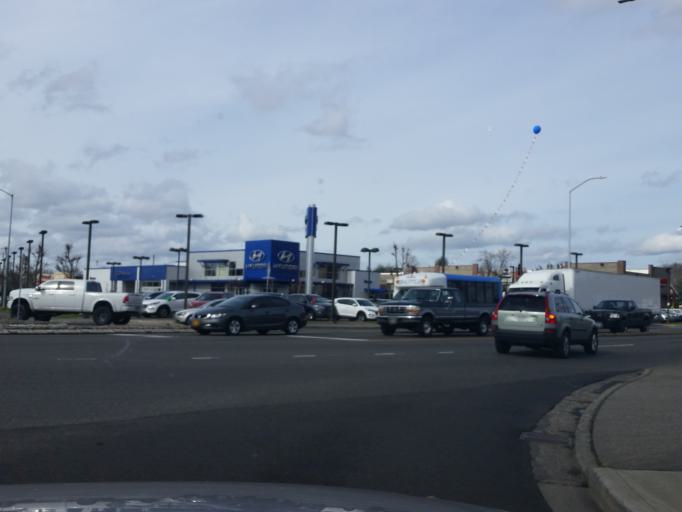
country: US
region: Washington
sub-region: Pierce County
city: Puyallup
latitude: 47.1988
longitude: -122.2936
